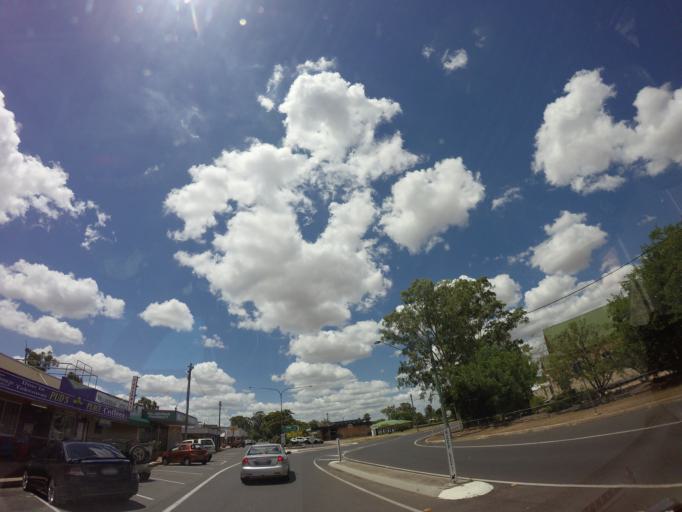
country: AU
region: Queensland
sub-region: Toowoomba
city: Oakey
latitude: -27.8771
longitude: 151.2697
